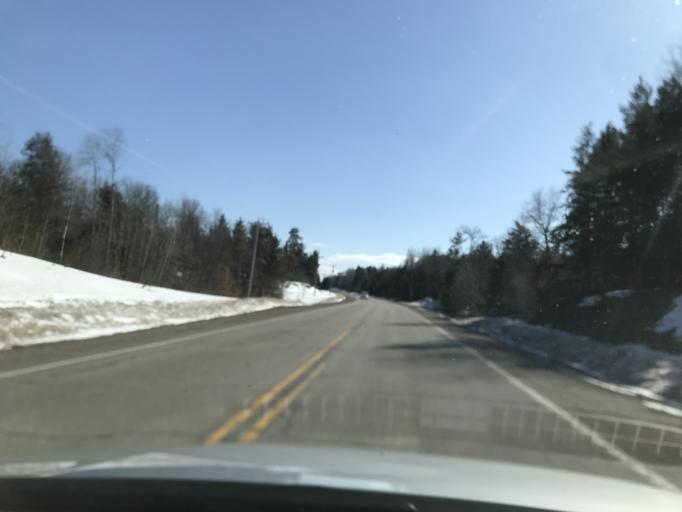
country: US
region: Wisconsin
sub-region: Marinette County
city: Peshtigo
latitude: 45.3341
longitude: -88.1015
